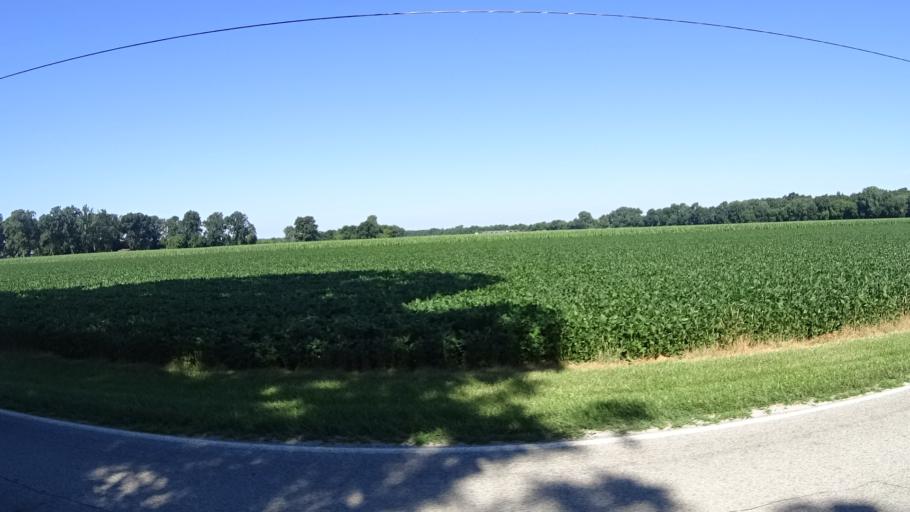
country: US
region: Ohio
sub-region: Erie County
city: Huron
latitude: 41.3662
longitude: -82.6144
